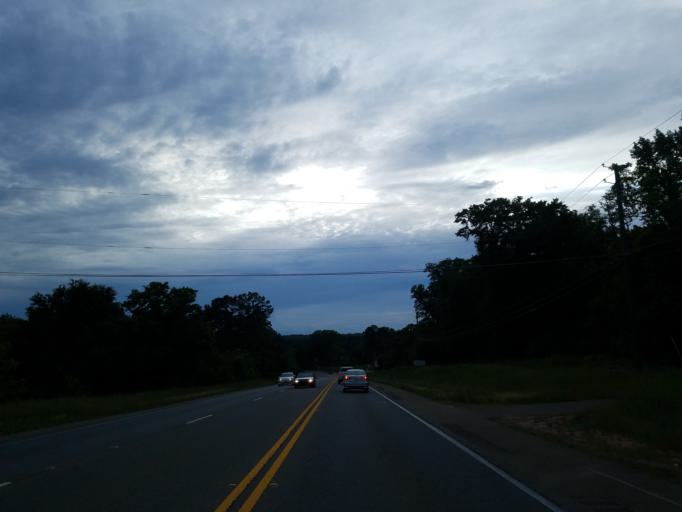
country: US
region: Georgia
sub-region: Cherokee County
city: Ball Ground
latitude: 34.2486
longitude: -84.3078
